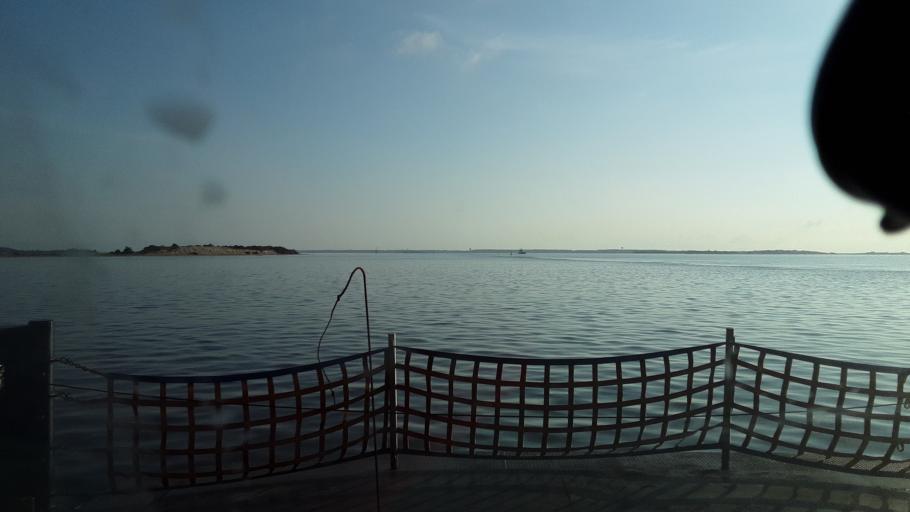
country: US
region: North Carolina
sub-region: Brunswick County
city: Southport
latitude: 33.9486
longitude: -77.9671
